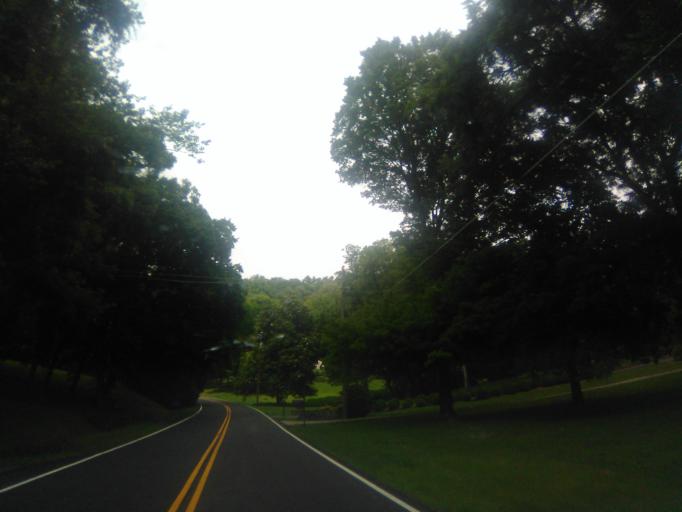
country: US
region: Tennessee
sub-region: Davidson County
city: Forest Hills
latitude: 36.0671
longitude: -86.8548
